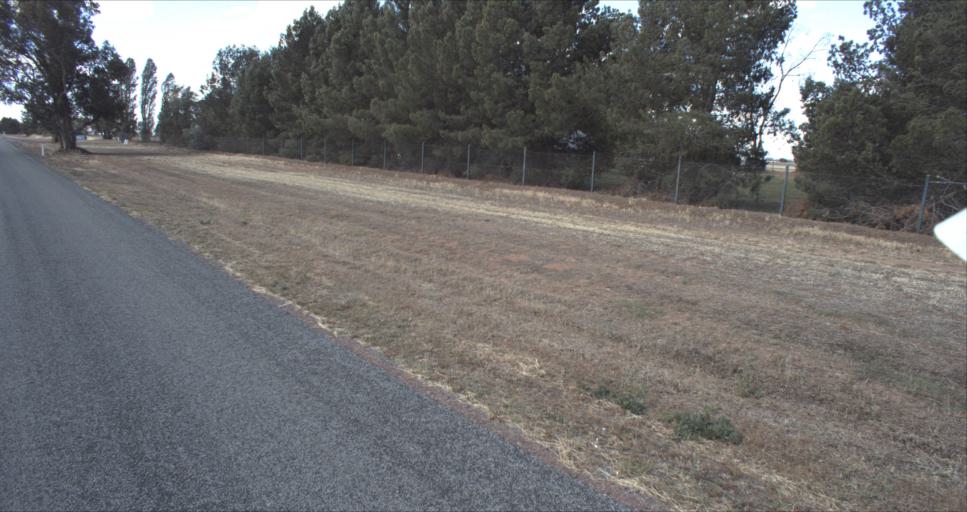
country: AU
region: New South Wales
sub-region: Leeton
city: Leeton
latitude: -34.4855
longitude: 146.2483
